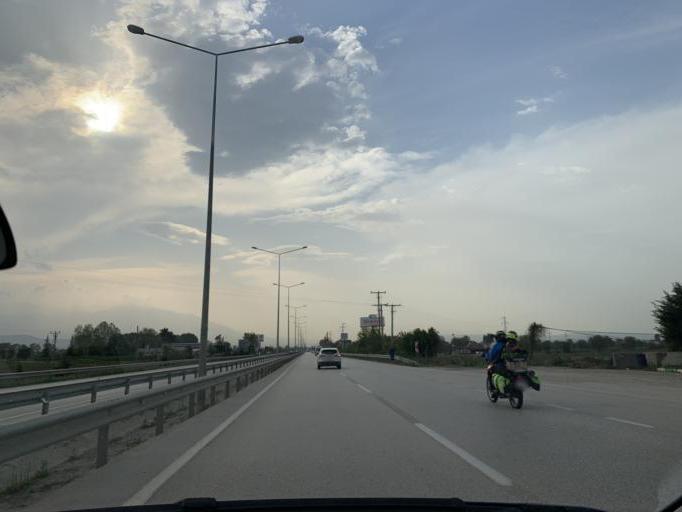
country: TR
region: Bursa
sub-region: Inegoel
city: Inegol
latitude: 40.0610
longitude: 29.5794
